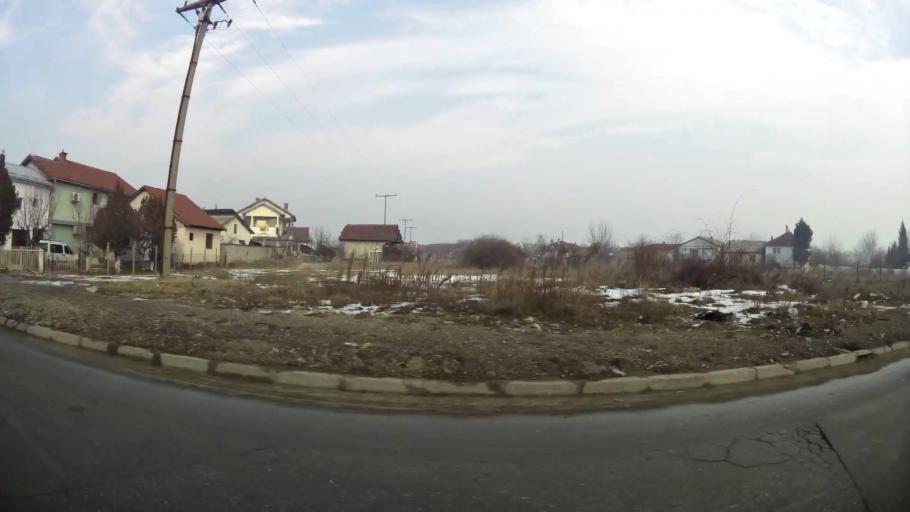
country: MK
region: Kisela Voda
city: Kisela Voda
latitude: 41.9892
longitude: 21.4985
